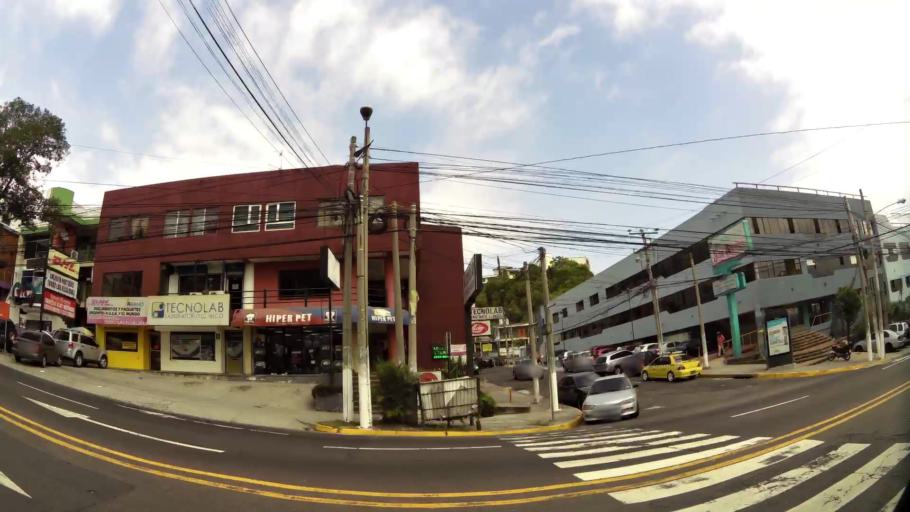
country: SV
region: La Libertad
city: Antiguo Cuscatlan
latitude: 13.7034
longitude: -89.2475
